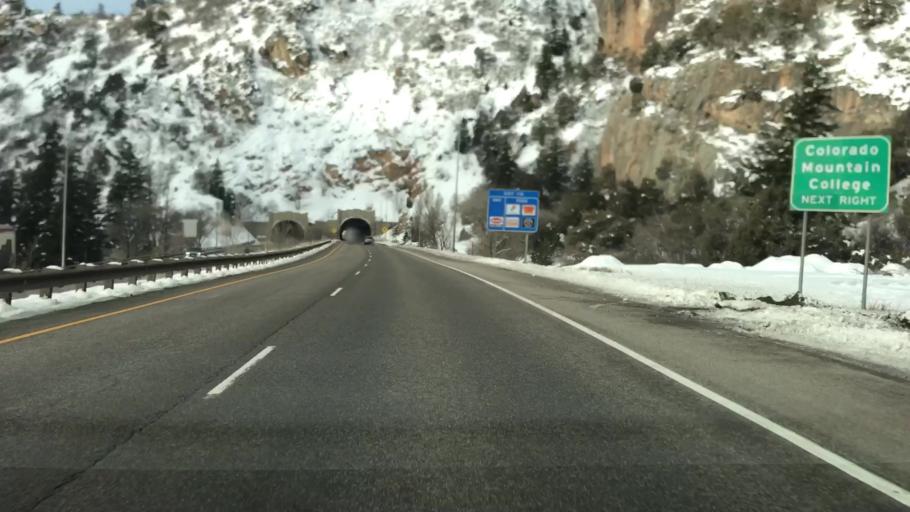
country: US
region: Colorado
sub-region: Garfield County
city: Glenwood Springs
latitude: 39.5622
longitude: -107.3030
